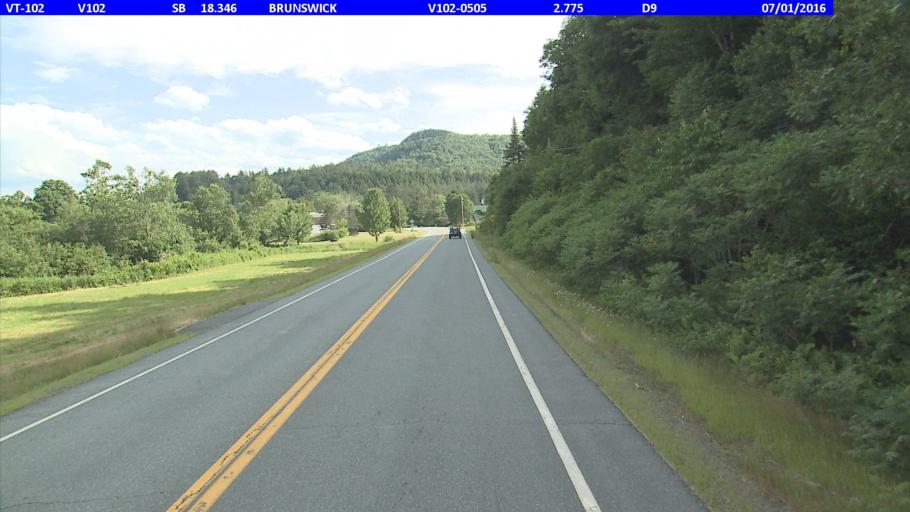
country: US
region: New Hampshire
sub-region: Coos County
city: Stratford
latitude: 44.6991
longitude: -71.6027
